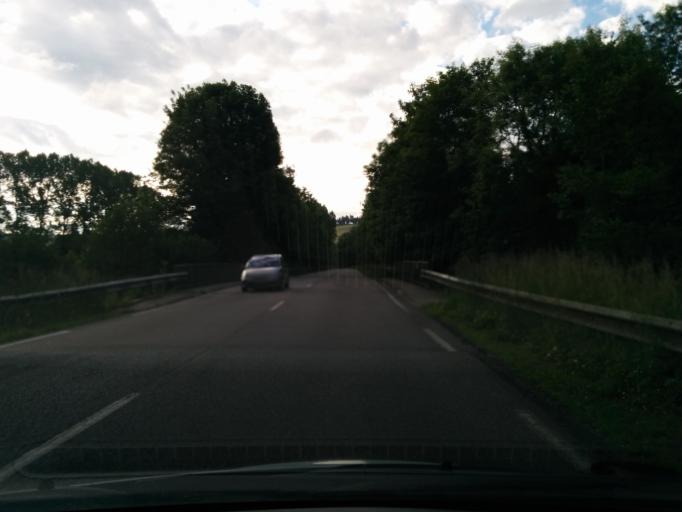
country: FR
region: Haute-Normandie
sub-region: Departement de l'Eure
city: Gasny
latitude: 49.0864
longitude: 1.6046
